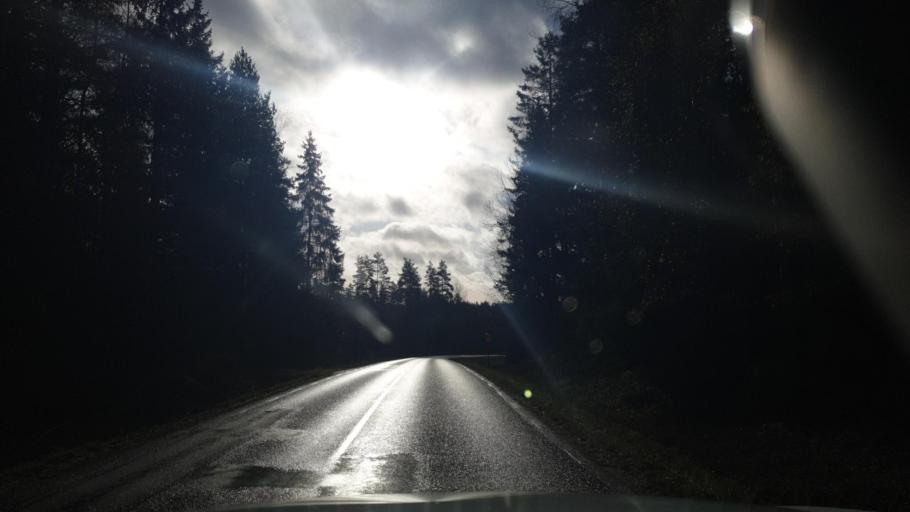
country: SE
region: Vaermland
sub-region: Grums Kommun
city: Grums
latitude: 59.4465
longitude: 12.9757
